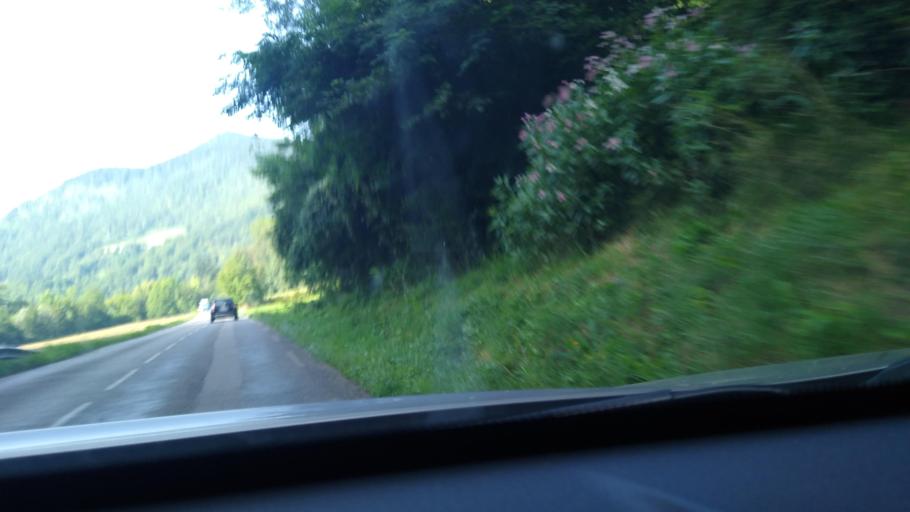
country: FR
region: Midi-Pyrenees
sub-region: Departement de l'Ariege
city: Saint-Girons
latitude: 42.9536
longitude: 1.1763
